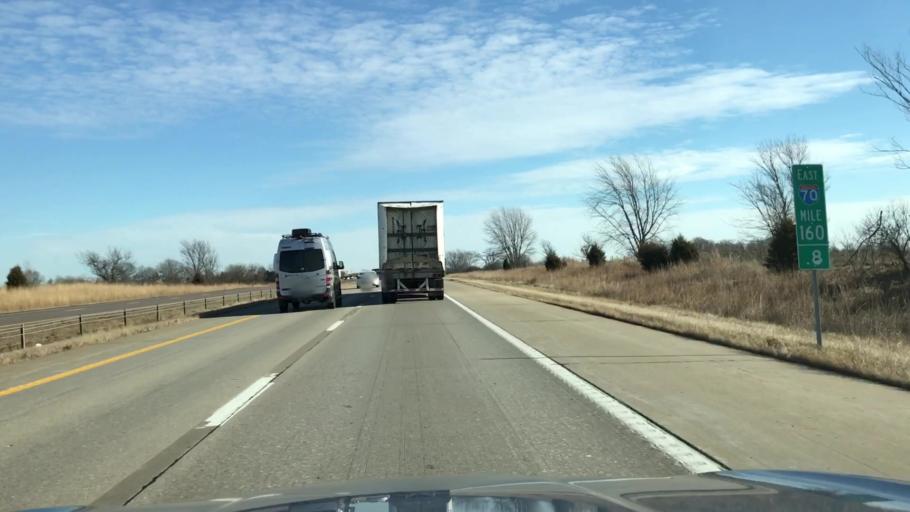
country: US
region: Missouri
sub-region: Montgomery County
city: Wellsville
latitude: 38.9115
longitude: -91.7119
